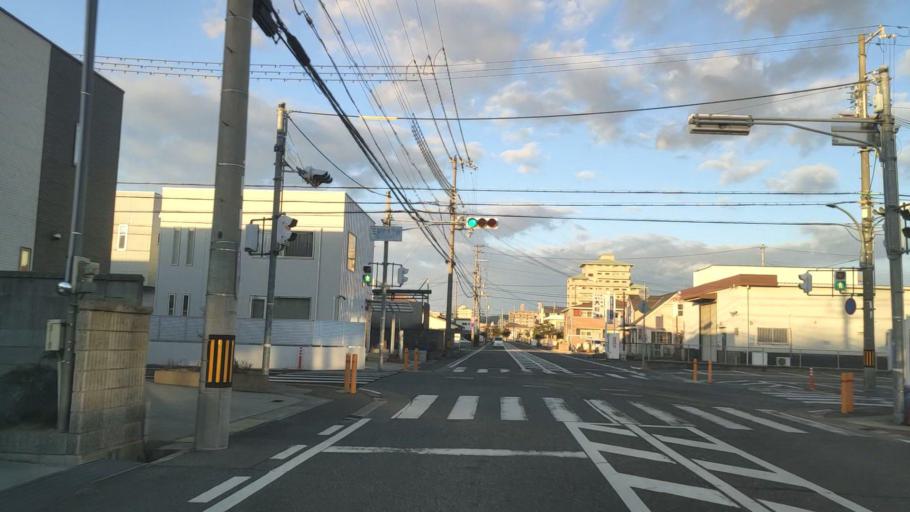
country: JP
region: Hyogo
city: Himeji
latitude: 34.8120
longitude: 134.6883
